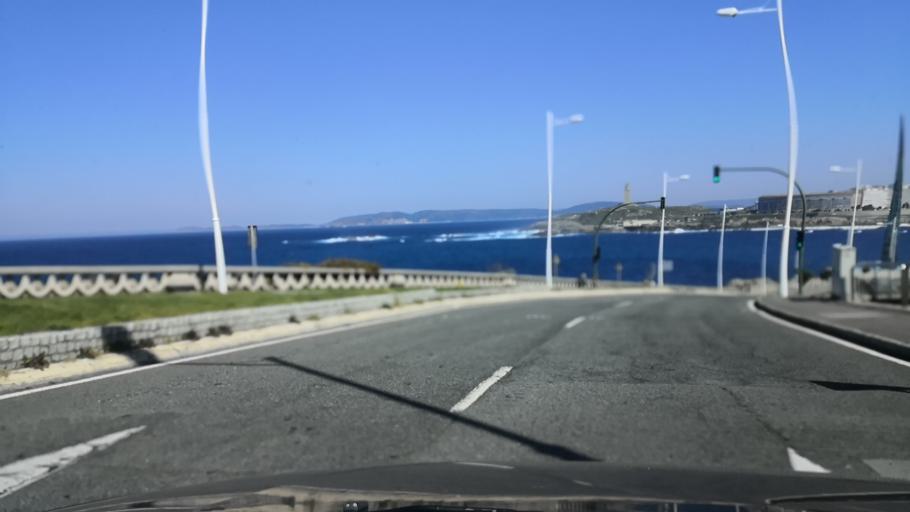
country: ES
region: Galicia
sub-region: Provincia da Coruna
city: A Coruna
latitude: 43.3762
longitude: -8.4260
